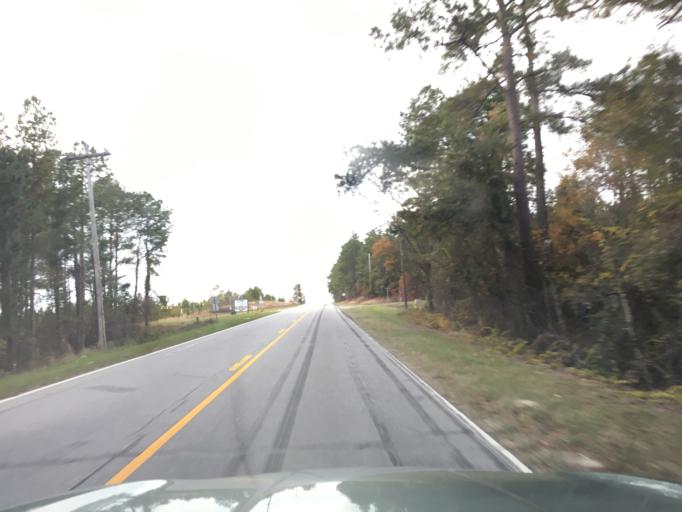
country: US
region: South Carolina
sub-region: Lexington County
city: Leesville
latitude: 33.8030
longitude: -81.4363
